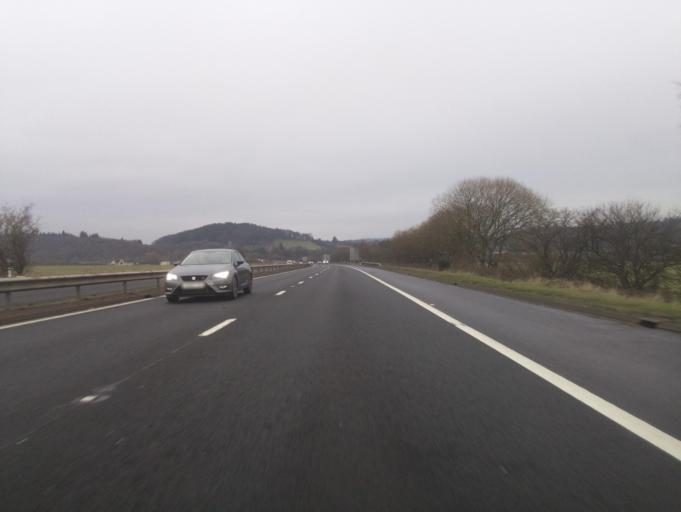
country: GB
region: Scotland
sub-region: Stirling
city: Bridge of Allan
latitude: 56.1483
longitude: -3.9682
